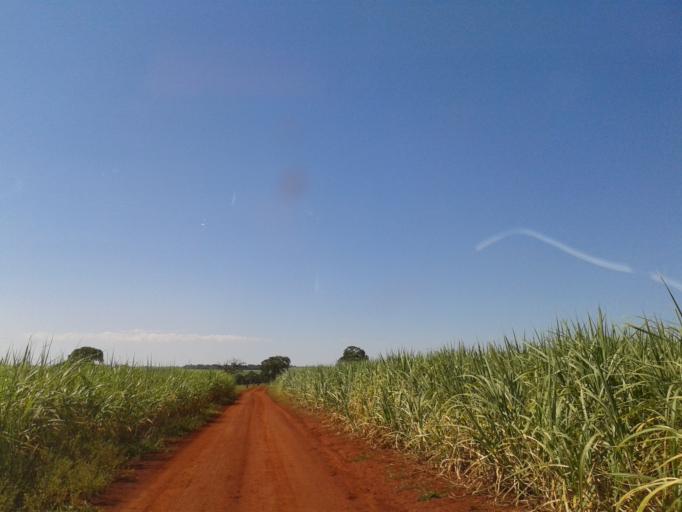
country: BR
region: Minas Gerais
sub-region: Centralina
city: Centralina
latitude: -18.6228
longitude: -49.2583
